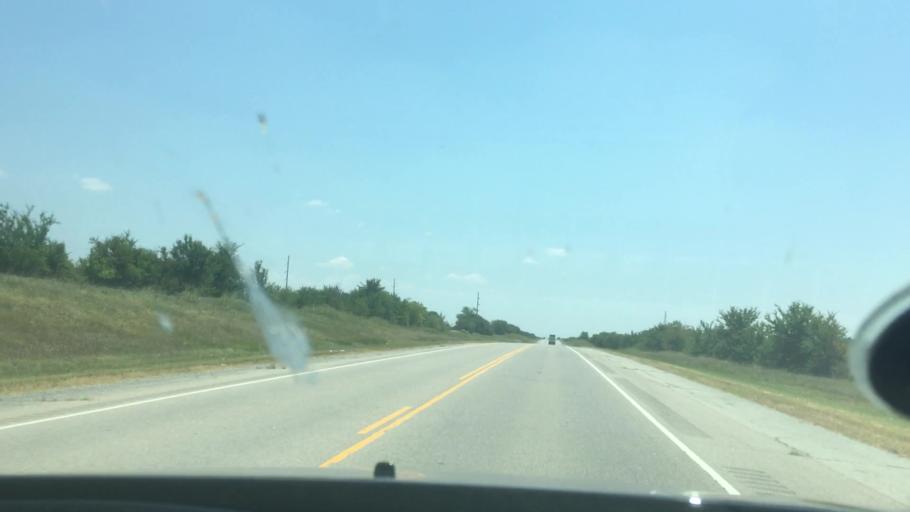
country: US
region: Oklahoma
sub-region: Pontotoc County
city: Ada
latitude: 34.6379
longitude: -96.4813
